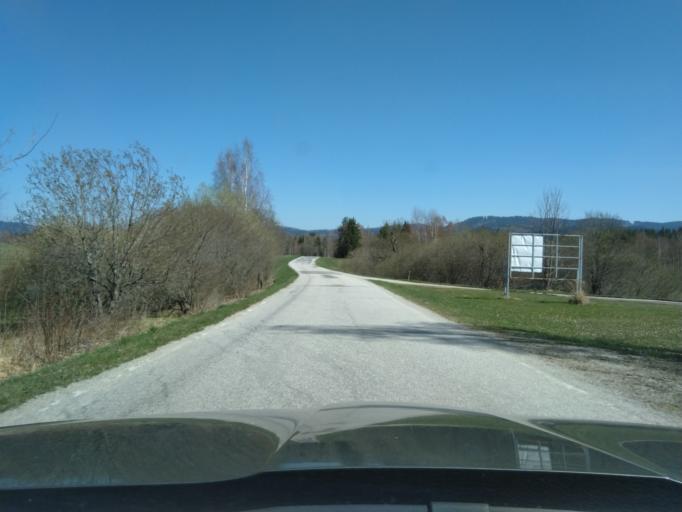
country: CZ
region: Jihocesky
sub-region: Okres Cesky Krumlov
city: Horni Plana
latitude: 48.7835
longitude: 13.9426
